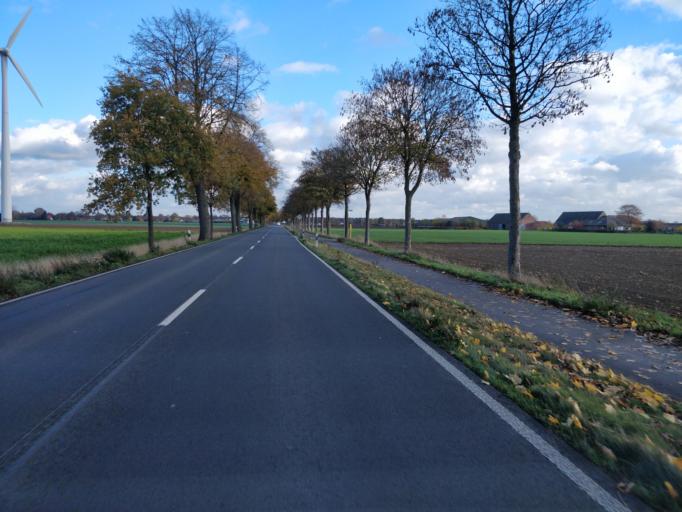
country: DE
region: North Rhine-Westphalia
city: Rees
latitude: 51.7754
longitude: 6.4383
